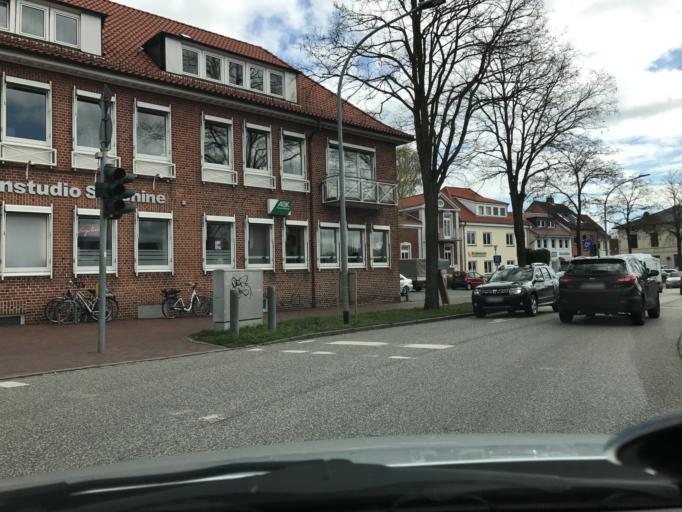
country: DE
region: Schleswig-Holstein
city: Neustadt in Holstein
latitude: 54.1067
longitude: 10.8107
